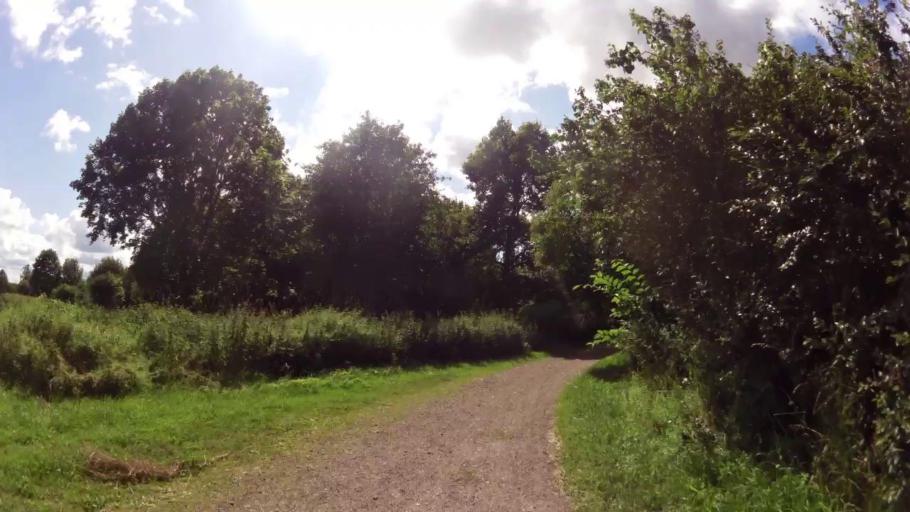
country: SE
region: OEstergoetland
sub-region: Linkopings Kommun
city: Berg
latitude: 58.4946
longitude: 15.5111
